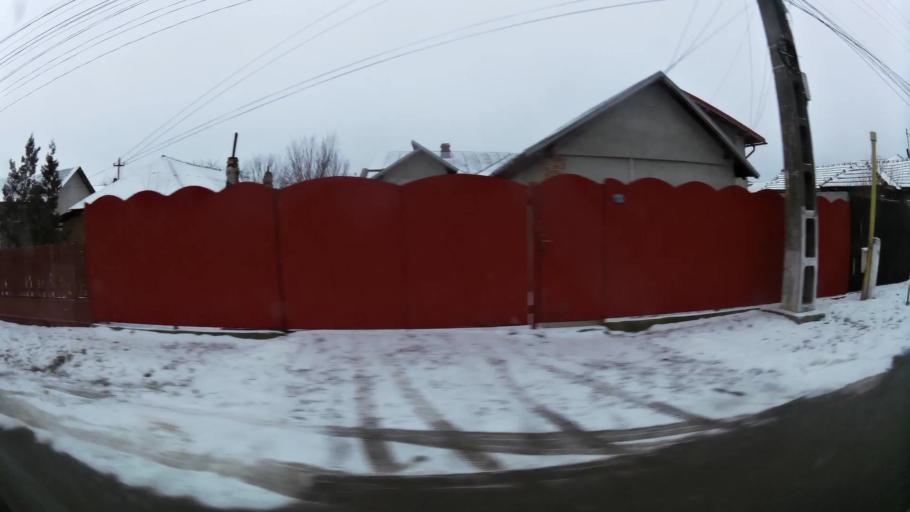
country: RO
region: Prahova
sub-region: Comuna Berceni
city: Corlatesti
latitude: 44.9120
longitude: 26.0860
